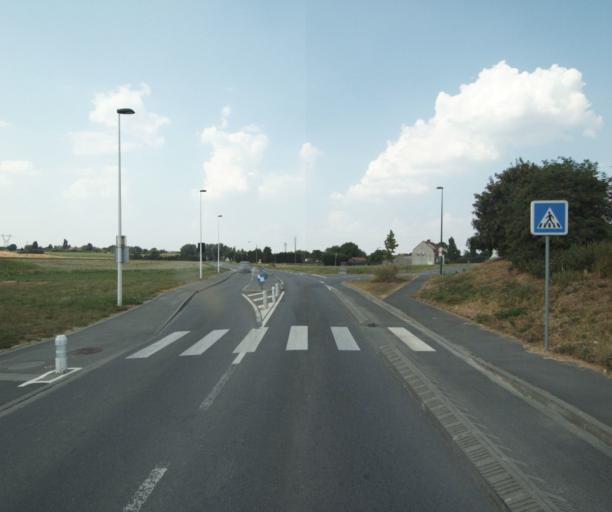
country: FR
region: Nord-Pas-de-Calais
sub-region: Departement du Nord
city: Linselles
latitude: 50.7248
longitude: 3.0809
